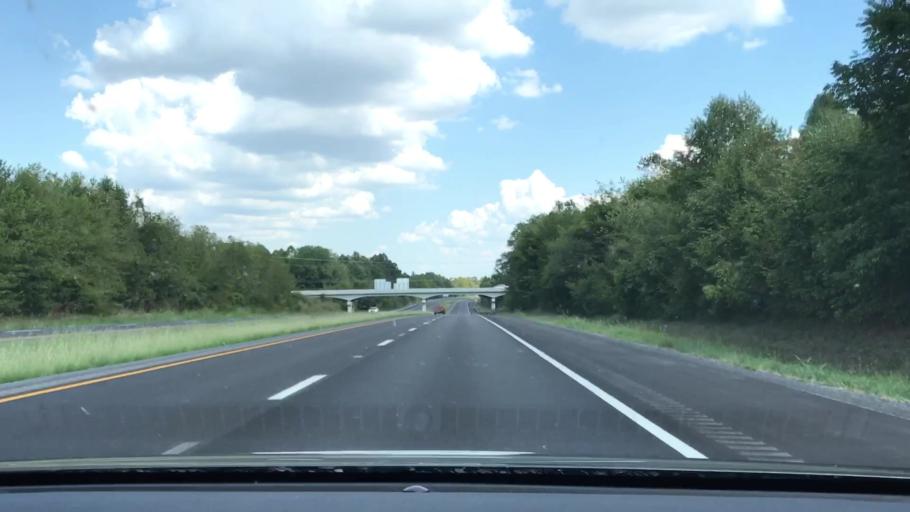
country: US
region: Kentucky
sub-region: Lyon County
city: Eddyville
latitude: 37.0783
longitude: -88.0761
